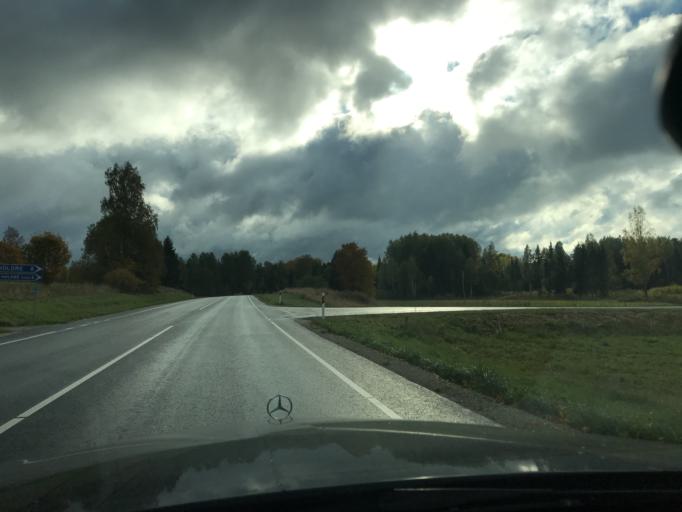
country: EE
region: Valgamaa
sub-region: Torva linn
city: Torva
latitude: 58.0072
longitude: 25.7605
